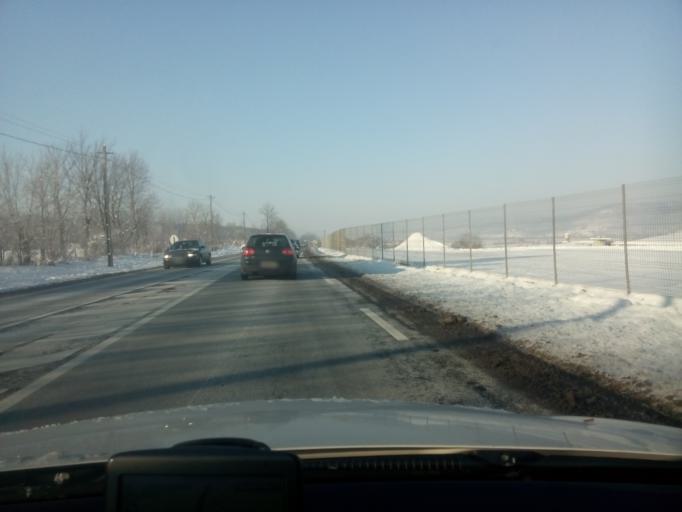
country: RO
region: Sibiu
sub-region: Comuna Talmaciu
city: Talmaciu
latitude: 45.6907
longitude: 24.2546
